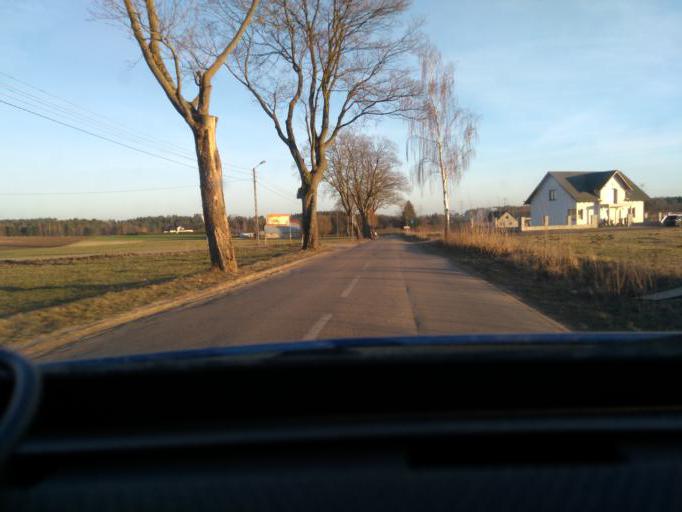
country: PL
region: Pomeranian Voivodeship
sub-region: Powiat kartuski
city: Przodkowo
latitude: 54.3973
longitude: 18.3367
